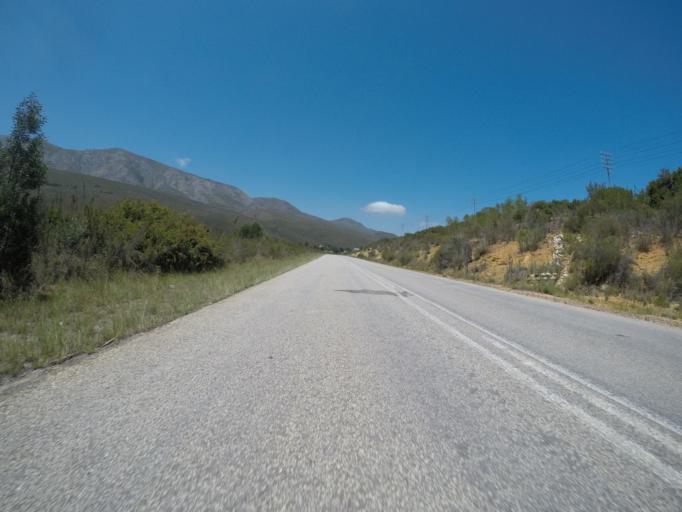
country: ZA
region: Eastern Cape
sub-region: Cacadu District Municipality
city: Kareedouw
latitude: -33.9135
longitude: 24.1828
